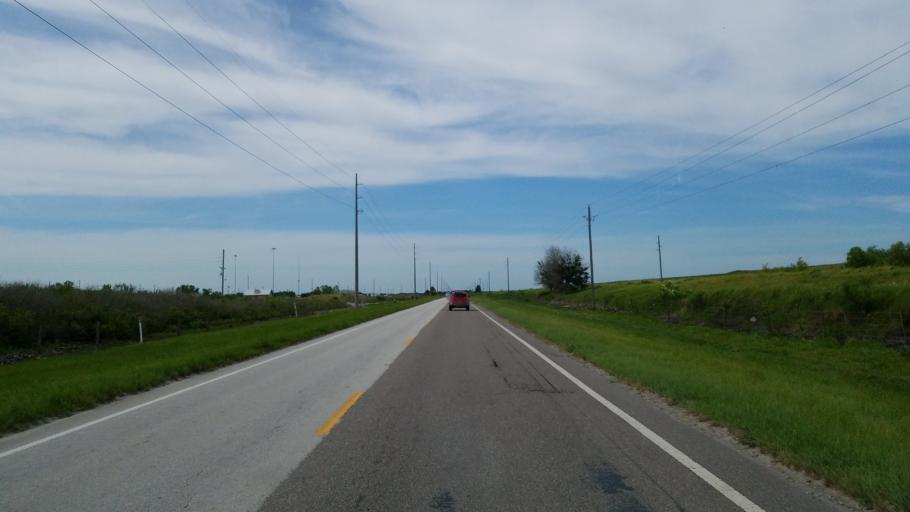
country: US
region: Florida
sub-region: Hillsborough County
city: Balm
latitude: 27.6503
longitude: -82.1463
